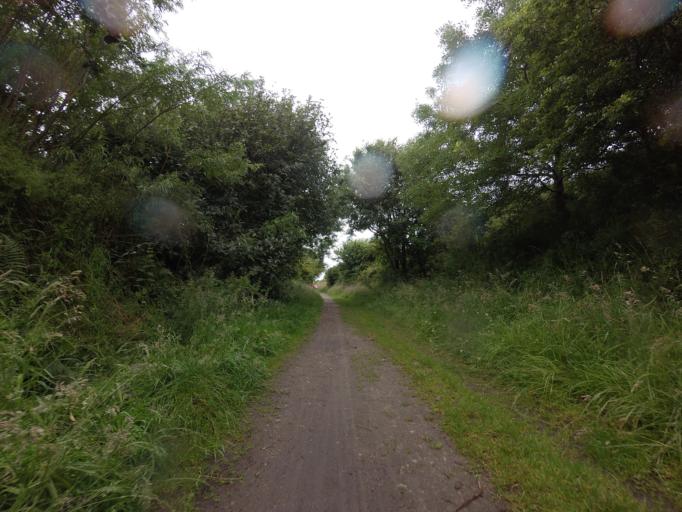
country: GB
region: Scotland
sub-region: Moray
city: Portknockie
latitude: 57.7009
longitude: -2.8539
